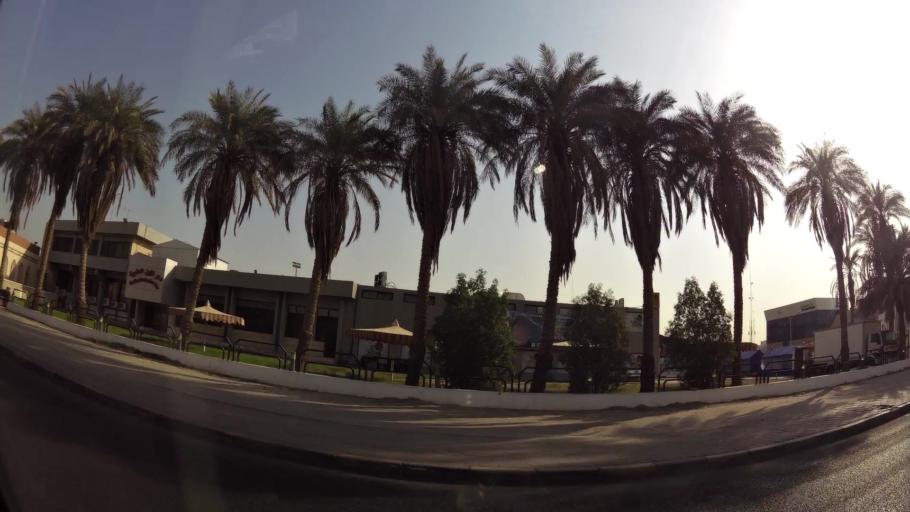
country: KW
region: Muhafazat Hawalli
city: Hawalli
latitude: 29.3256
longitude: 48.0303
